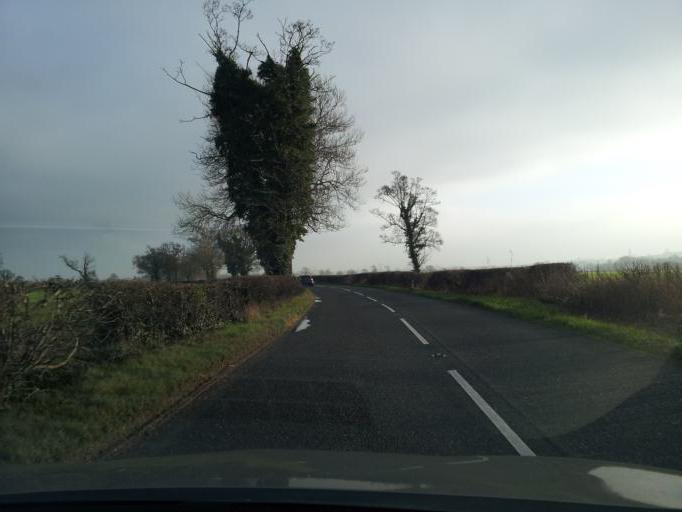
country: GB
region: England
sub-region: Derbyshire
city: Rodsley
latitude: 52.8745
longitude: -1.7326
